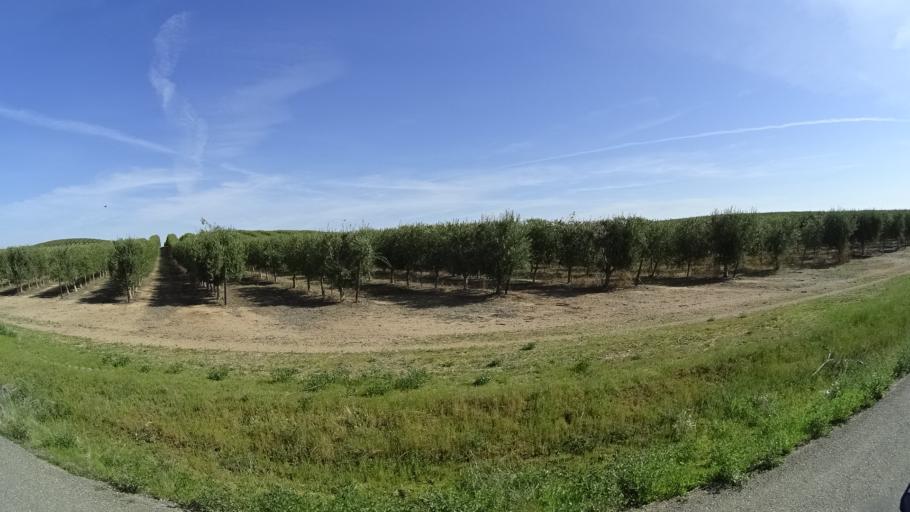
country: US
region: California
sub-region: Glenn County
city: Willows
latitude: 39.6142
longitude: -122.2913
